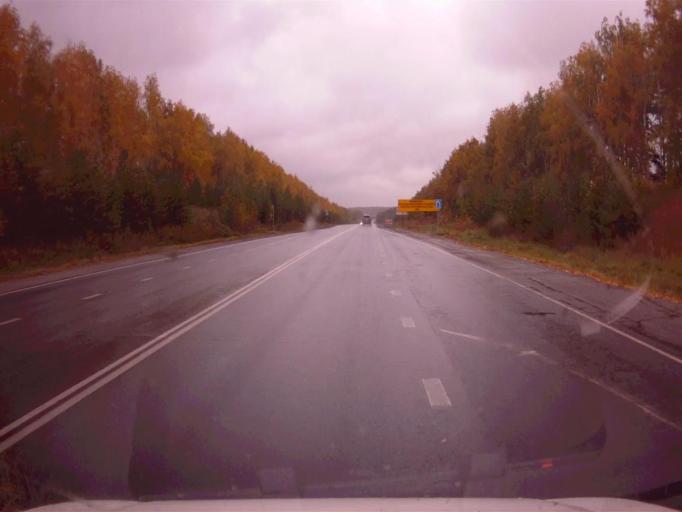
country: RU
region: Chelyabinsk
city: Roshchino
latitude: 55.3615
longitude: 61.2176
